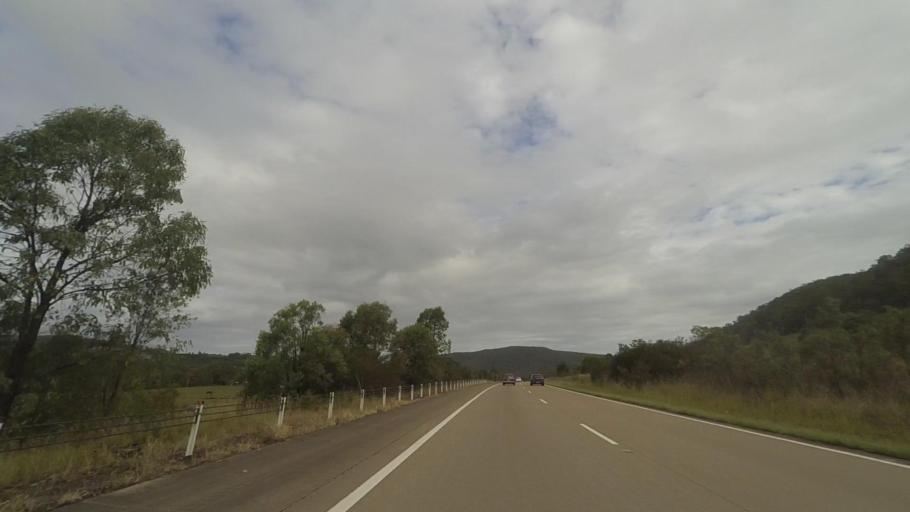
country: AU
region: New South Wales
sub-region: Port Stephens Shire
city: Port Stephens
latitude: -32.6262
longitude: 151.9882
